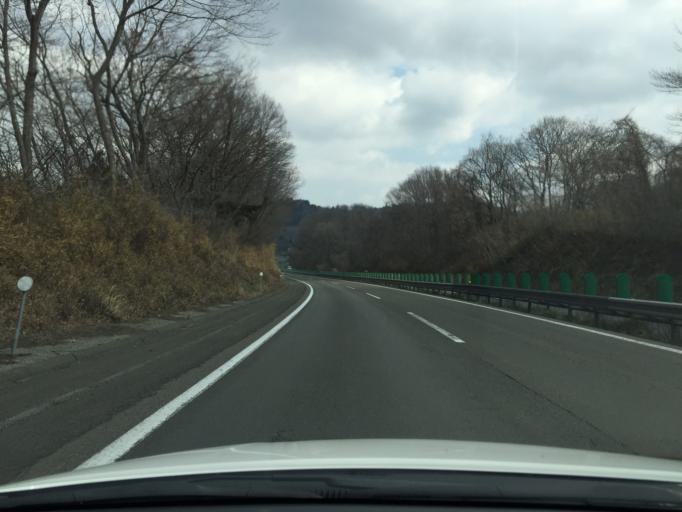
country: JP
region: Miyagi
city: Sendai
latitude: 38.2338
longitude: 140.8139
